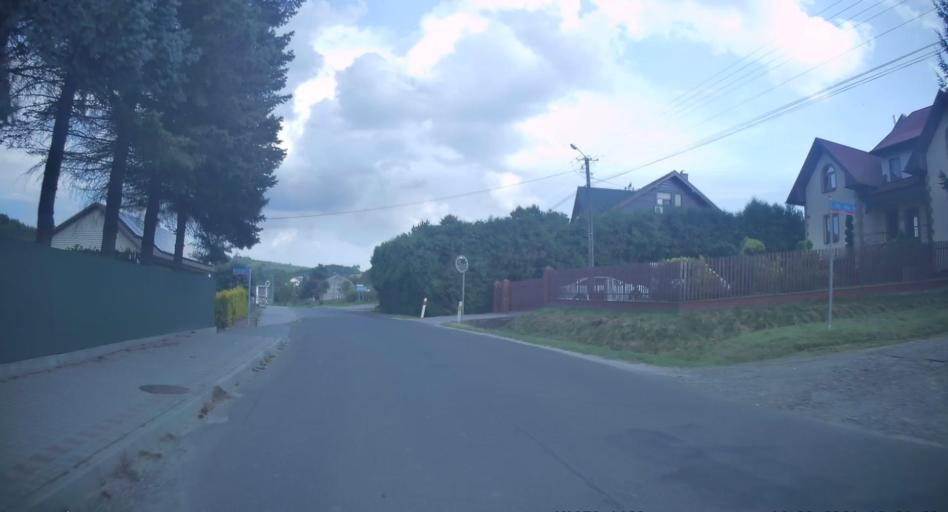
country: PL
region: Subcarpathian Voivodeship
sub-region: Powiat debicki
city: Debica
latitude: 49.9930
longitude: 21.4264
